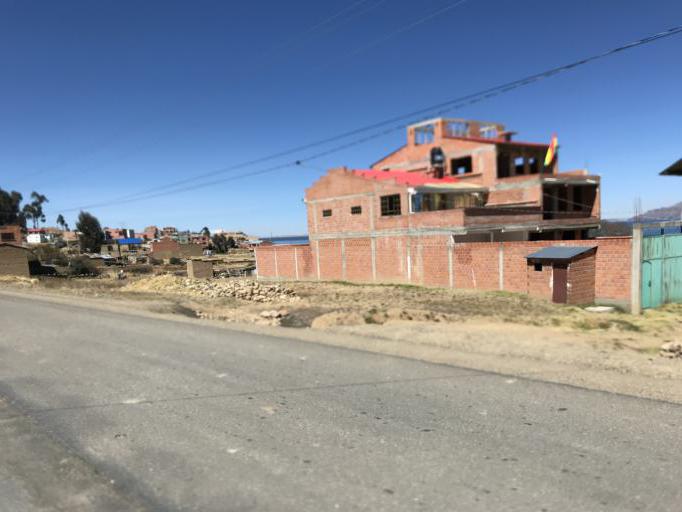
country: BO
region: La Paz
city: Huatajata
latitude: -16.2106
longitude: -68.6948
